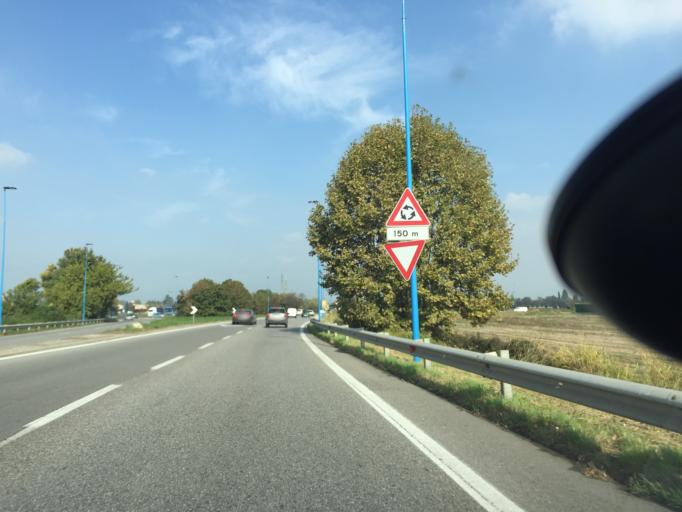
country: IT
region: Lombardy
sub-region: Provincia di Brescia
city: Castel Mella
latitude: 45.5058
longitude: 10.1657
